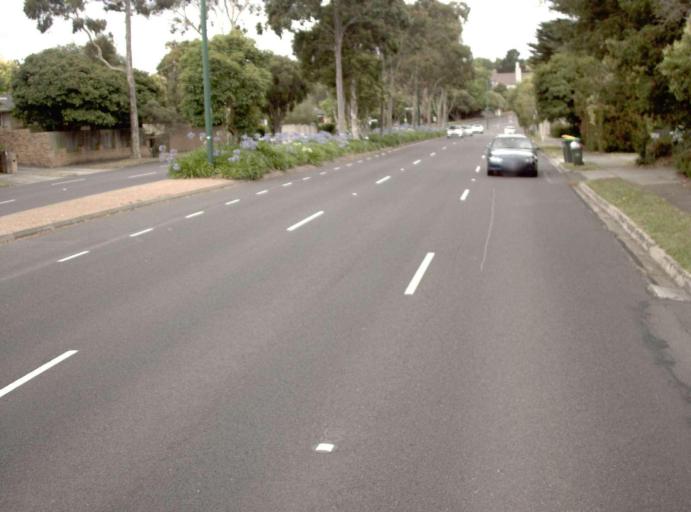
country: AU
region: Victoria
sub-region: Whitehorse
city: Blackburn
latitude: -37.8183
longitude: 145.1432
